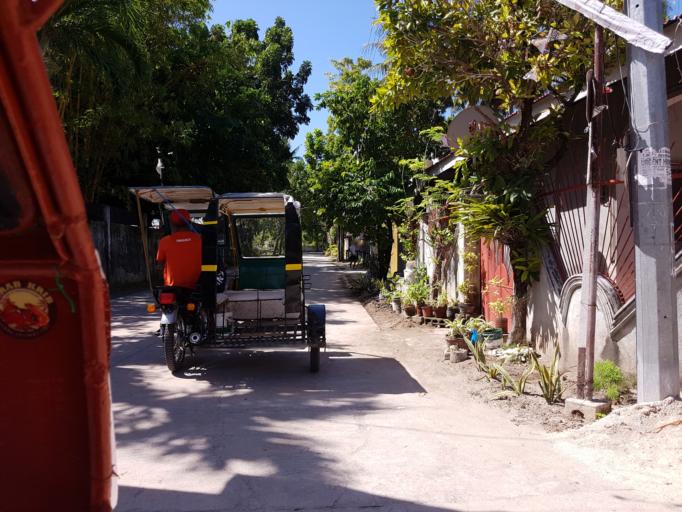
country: PH
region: Central Visayas
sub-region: Province of Cebu
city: Santa Fe
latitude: 11.1530
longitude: 123.8039
